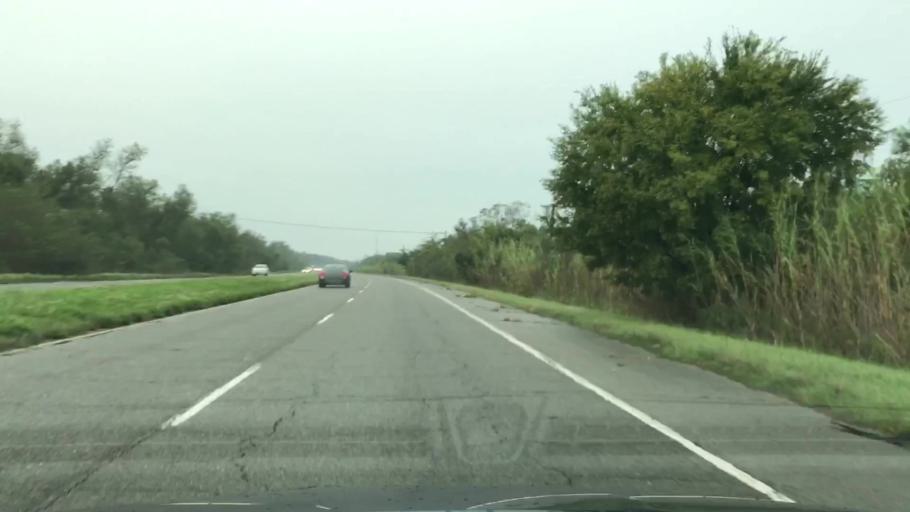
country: US
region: Louisiana
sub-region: Saint Charles Parish
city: Des Allemands
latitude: 29.7960
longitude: -90.5081
